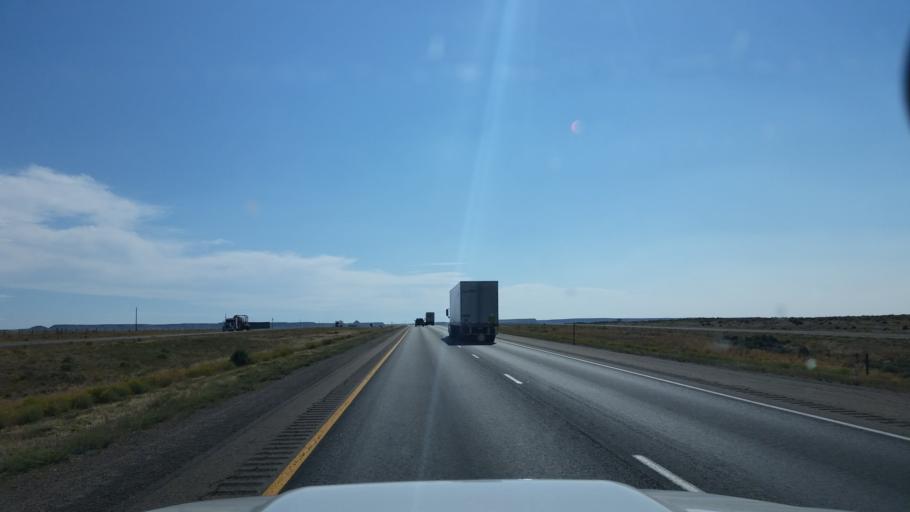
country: US
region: Wyoming
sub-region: Uinta County
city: Lyman
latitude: 41.5261
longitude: -109.9528
